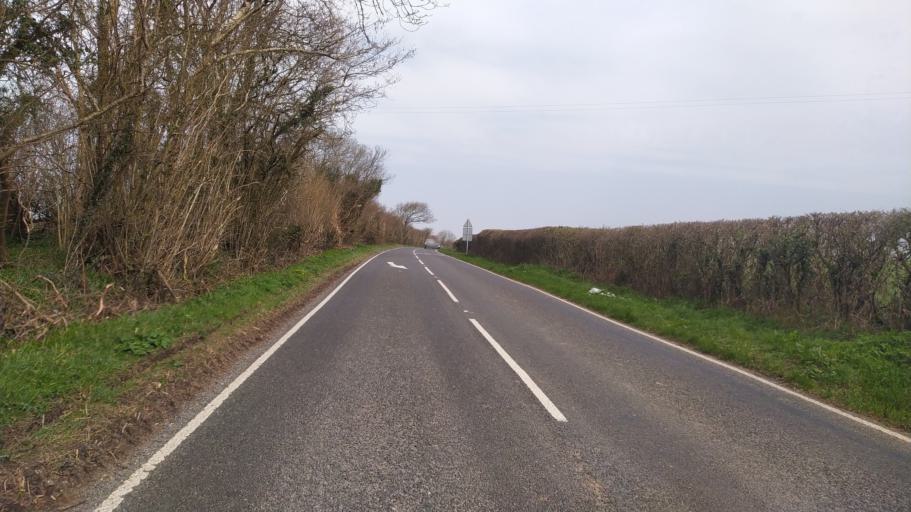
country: GB
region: England
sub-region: Dorset
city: Beaminster
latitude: 50.7910
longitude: -2.6212
